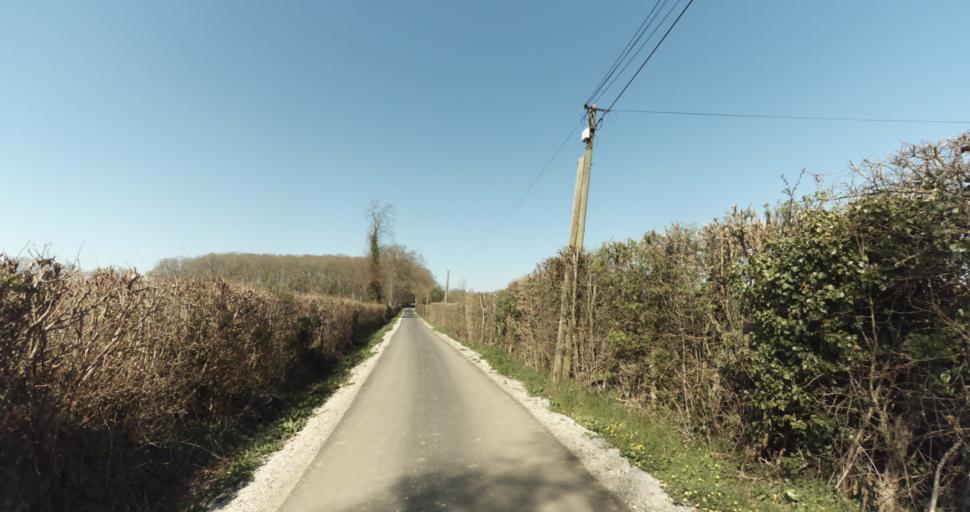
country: FR
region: Lower Normandy
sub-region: Departement du Calvados
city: Saint-Pierre-sur-Dives
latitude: 49.0060
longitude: 0.0009
